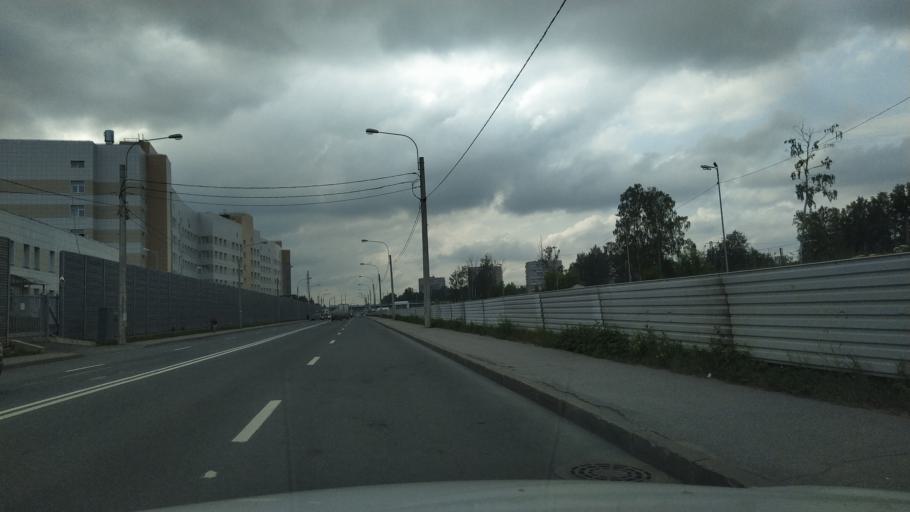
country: RU
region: St.-Petersburg
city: Krasnogvargeisky
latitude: 59.9854
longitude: 30.4378
